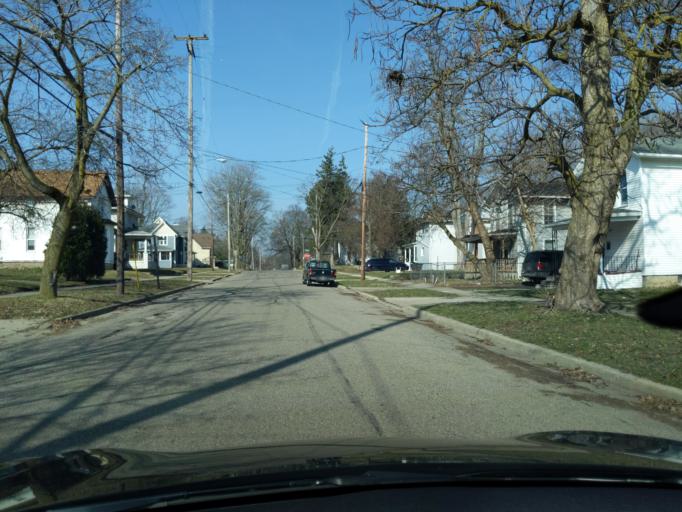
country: US
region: Michigan
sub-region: Jackson County
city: Jackson
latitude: 42.2413
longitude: -84.4136
